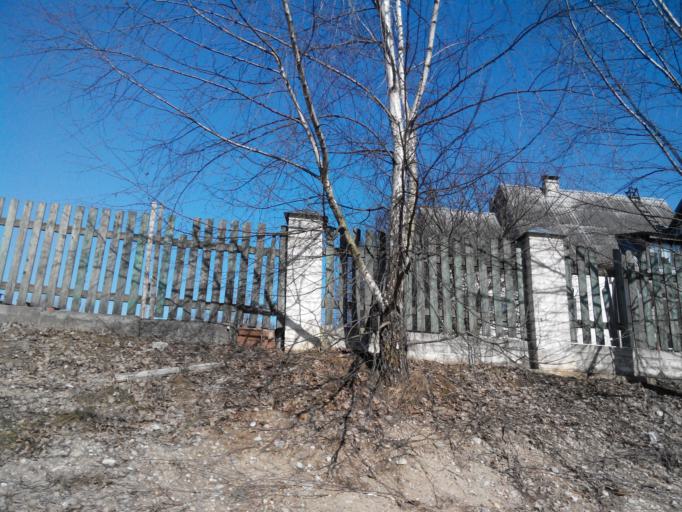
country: BY
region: Minsk
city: Zhdanovichy
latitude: 53.9151
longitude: 27.3941
